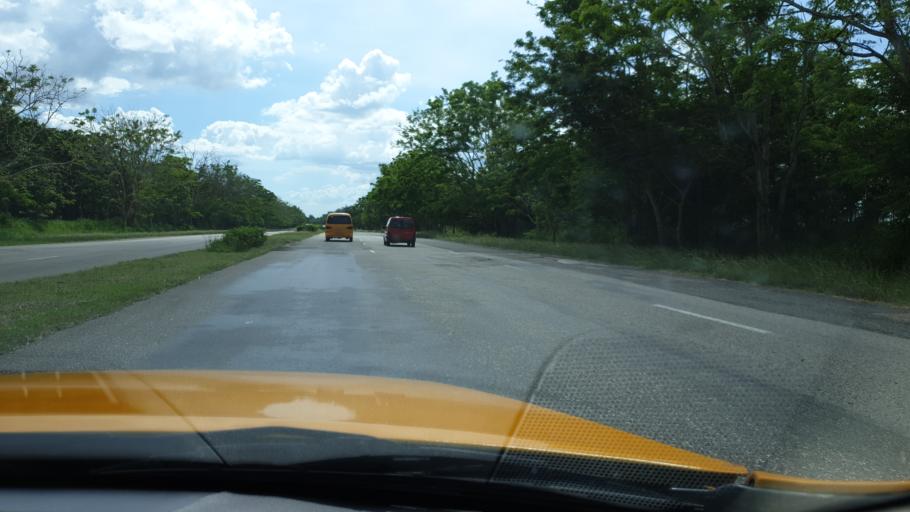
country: CU
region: Cienfuegos
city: Cruces
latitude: 22.4554
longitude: -80.3115
